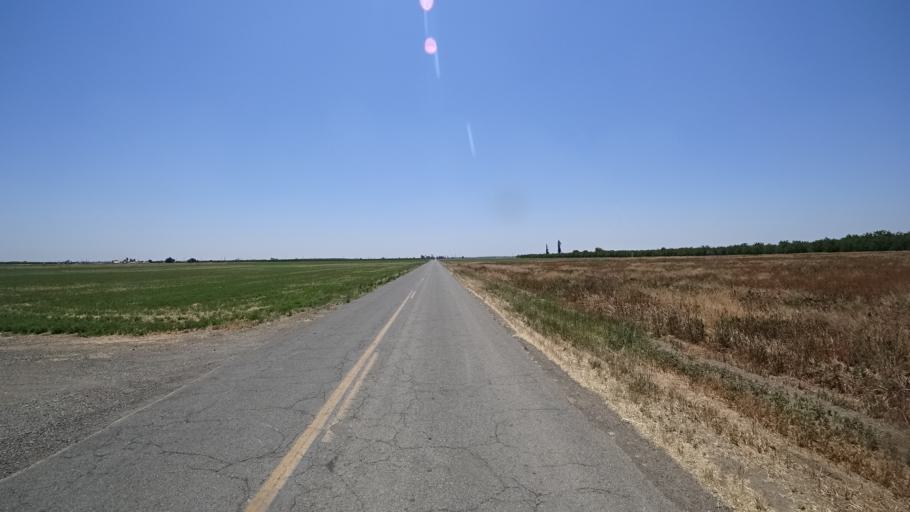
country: US
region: California
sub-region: Kings County
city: Lucerne
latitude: 36.3784
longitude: -119.7269
